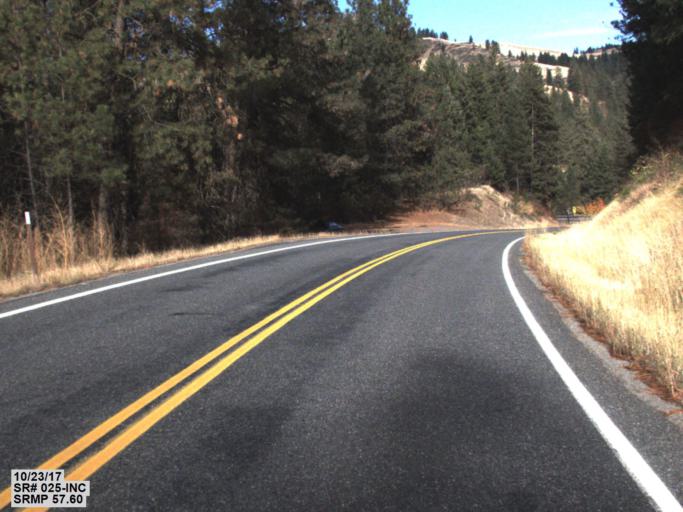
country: US
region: Washington
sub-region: Stevens County
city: Kettle Falls
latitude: 48.3054
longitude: -118.1487
